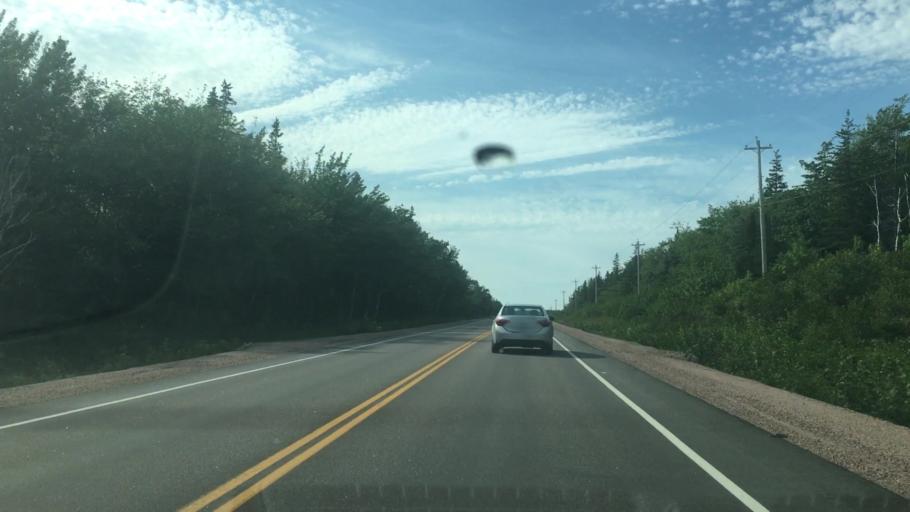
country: CA
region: Nova Scotia
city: Sydney Mines
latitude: 46.8188
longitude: -60.3494
